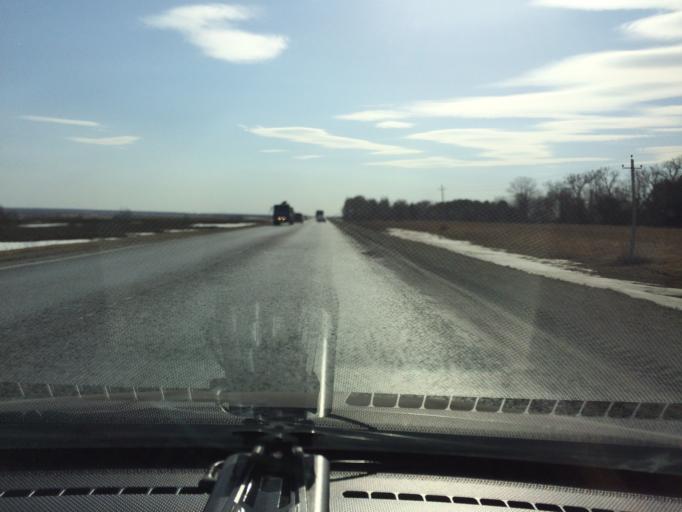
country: RU
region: Mariy-El
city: Yoshkar-Ola
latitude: 56.7059
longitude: 48.0770
